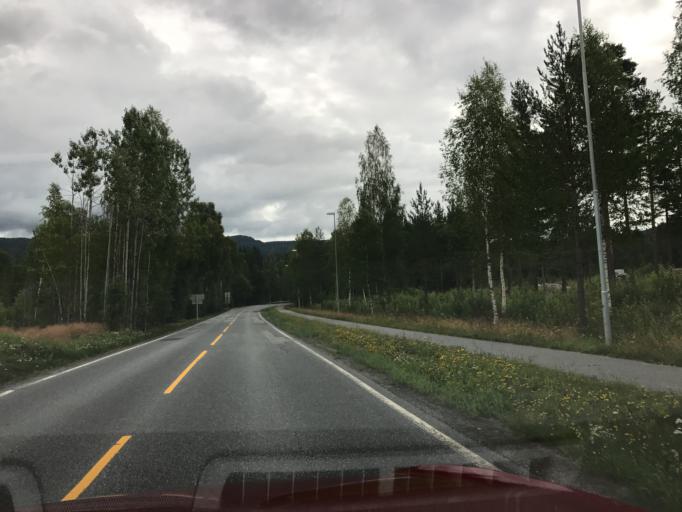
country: NO
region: Buskerud
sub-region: Rollag
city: Rollag
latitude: 60.0394
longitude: 9.1675
